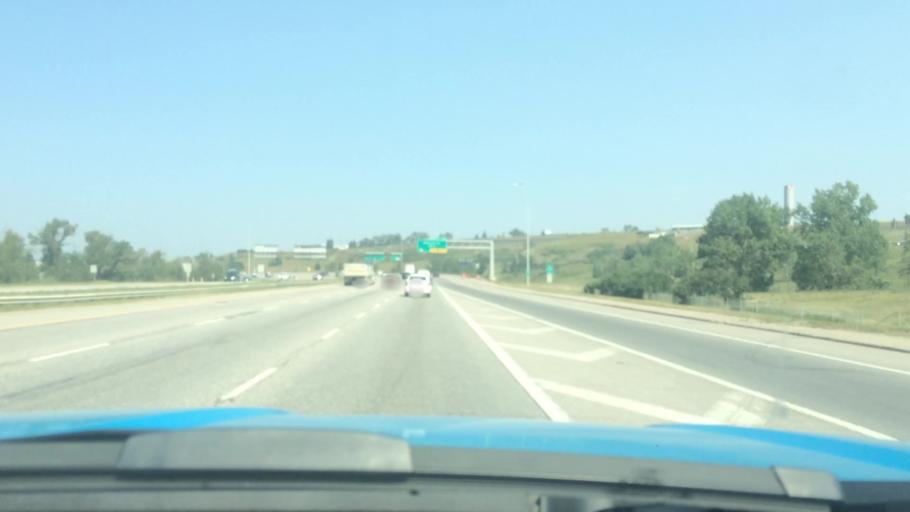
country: CA
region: Alberta
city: Calgary
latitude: 51.0400
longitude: -114.0063
